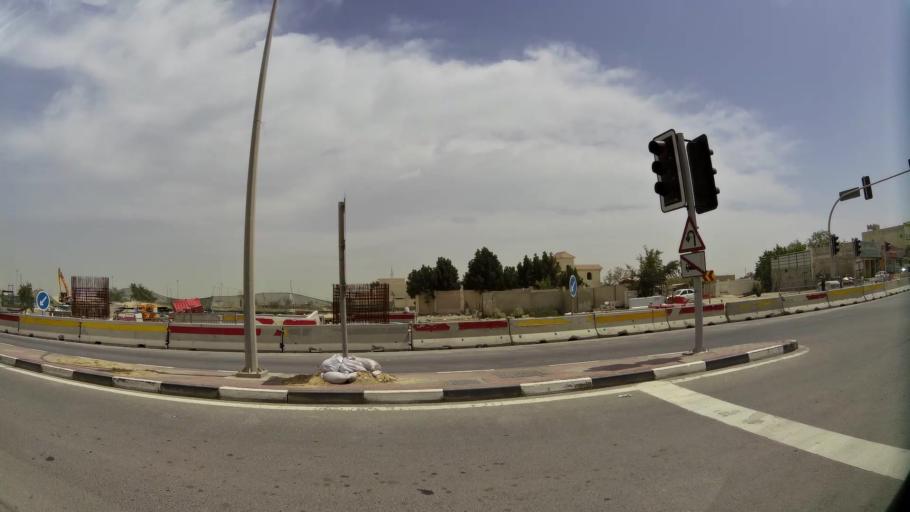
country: QA
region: Baladiyat ar Rayyan
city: Ar Rayyan
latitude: 25.2999
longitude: 51.4202
